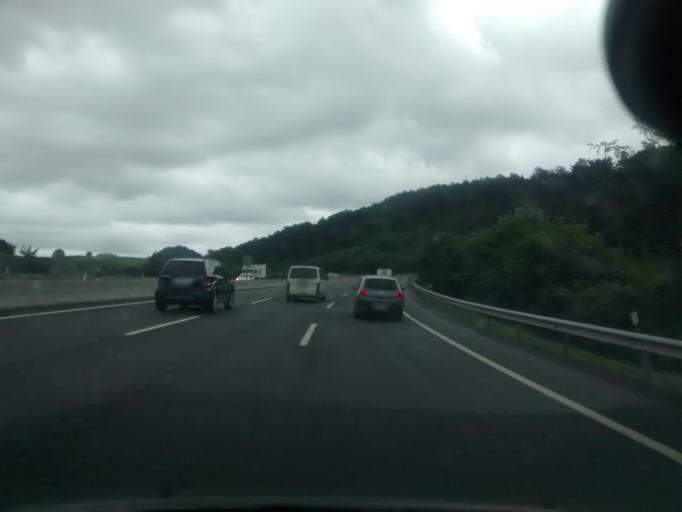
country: ES
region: Basque Country
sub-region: Provincia de Guipuzcoa
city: Orio
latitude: 43.2868
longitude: -2.0923
